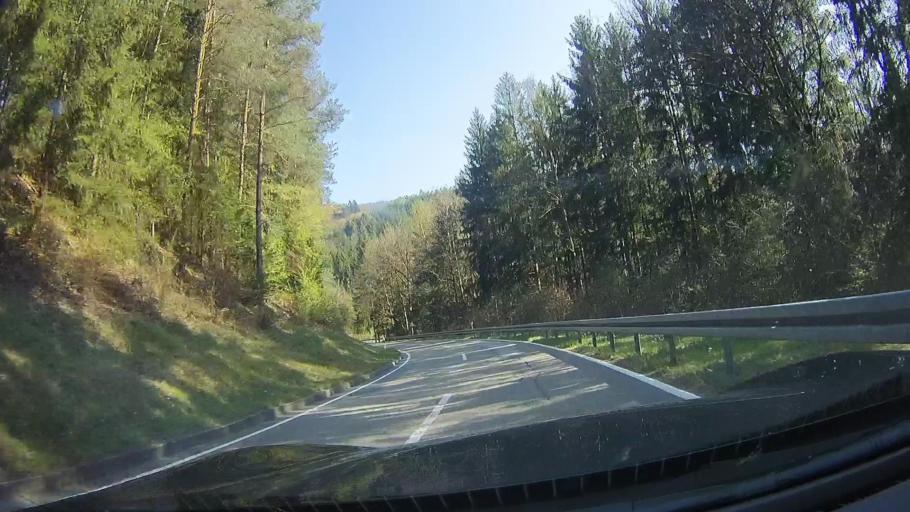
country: DE
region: Hesse
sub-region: Regierungsbezirk Darmstadt
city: Rothenberg
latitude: 49.4743
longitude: 8.9045
